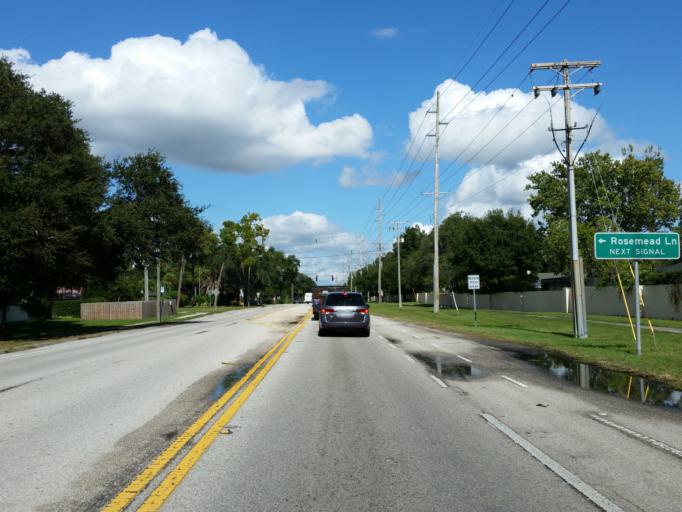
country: US
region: Florida
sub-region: Hillsborough County
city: Bloomingdale
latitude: 27.8855
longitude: -82.2693
